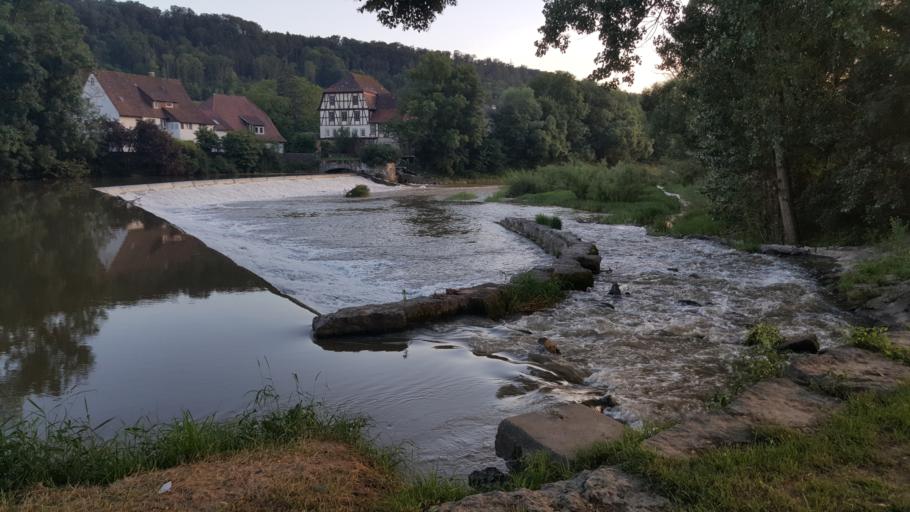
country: DE
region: Baden-Wuerttemberg
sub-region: Regierungsbezirk Stuttgart
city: Forchtenberg
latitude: 49.2894
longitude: 9.5622
